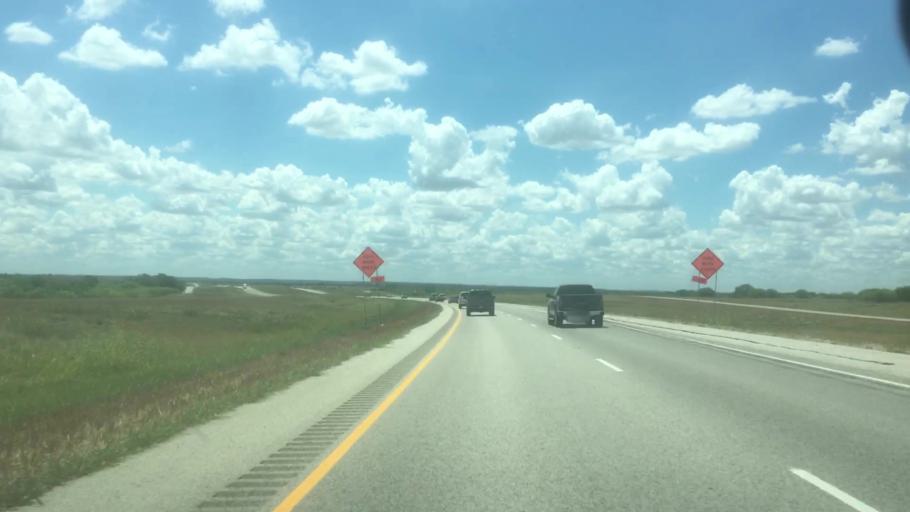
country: US
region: Texas
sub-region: Caldwell County
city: Martindale
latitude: 29.8052
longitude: -97.7749
